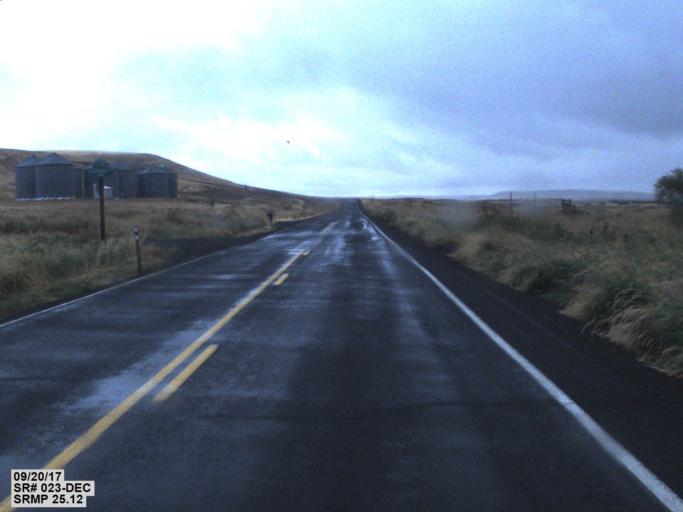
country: US
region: Washington
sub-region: Spokane County
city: Cheney
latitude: 47.1176
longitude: -117.7860
